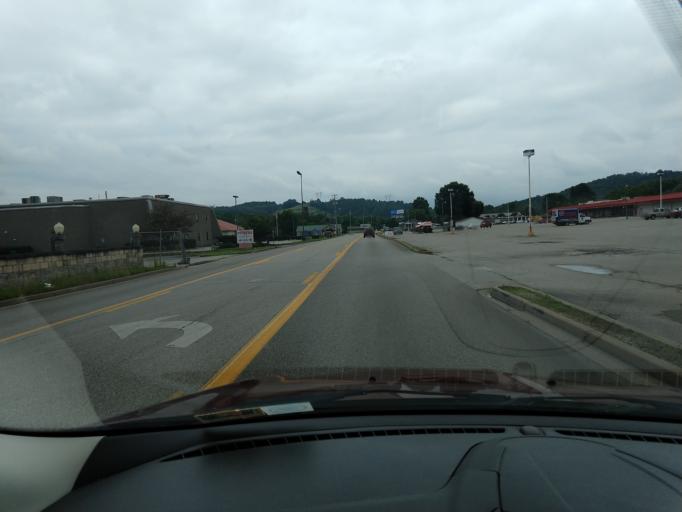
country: US
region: West Virginia
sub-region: Jackson County
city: Ripley
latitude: 38.8232
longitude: -81.7236
